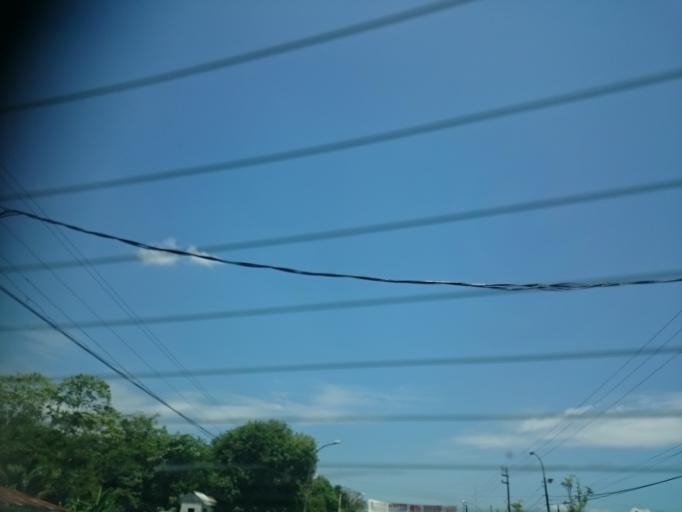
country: PE
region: Loreto
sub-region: Provincia de Maynas
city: Iquitos
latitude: -3.7675
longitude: -73.2740
